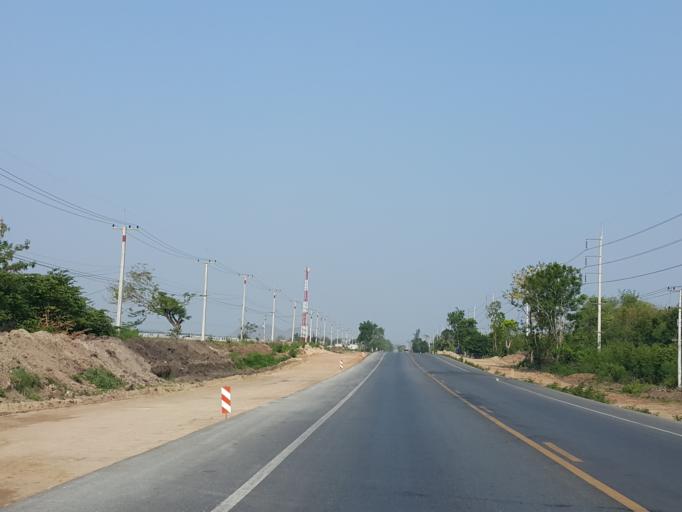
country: TH
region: Kanchanaburi
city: Sai Yok
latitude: 14.0882
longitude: 99.3298
